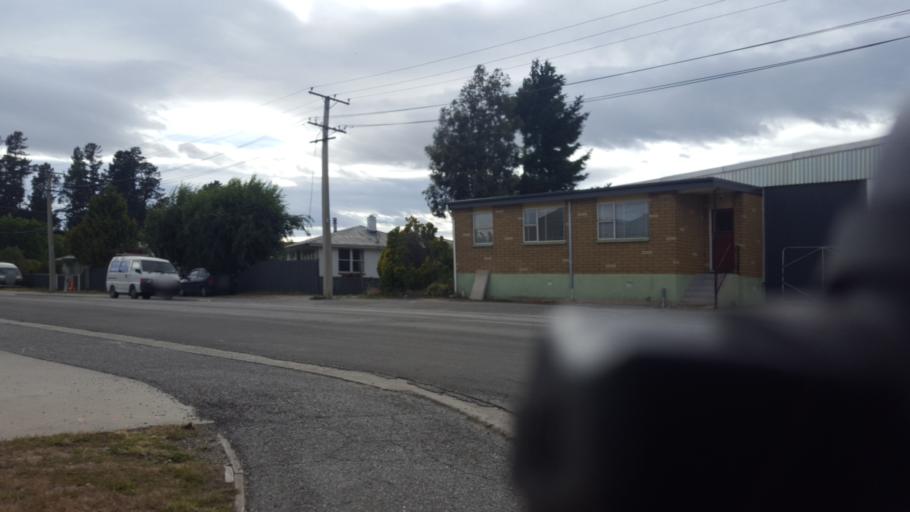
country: NZ
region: Otago
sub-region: Queenstown-Lakes District
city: Wanaka
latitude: -45.2456
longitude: 169.3955
